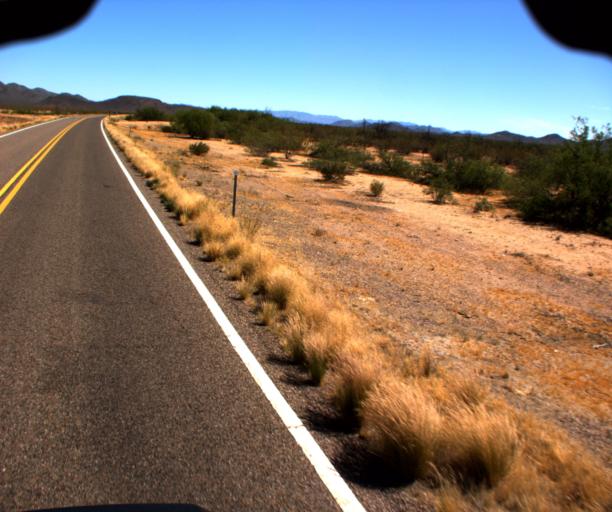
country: US
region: Arizona
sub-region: Yavapai County
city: Congress
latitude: 33.9864
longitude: -113.1366
